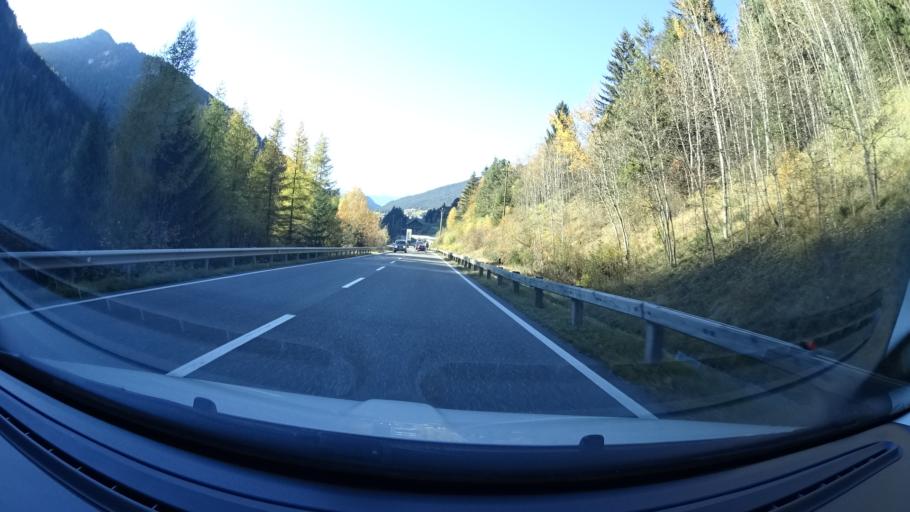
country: IT
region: Trentino-Alto Adige
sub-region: Bolzano
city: Ortisei
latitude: 46.5651
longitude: 11.6935
